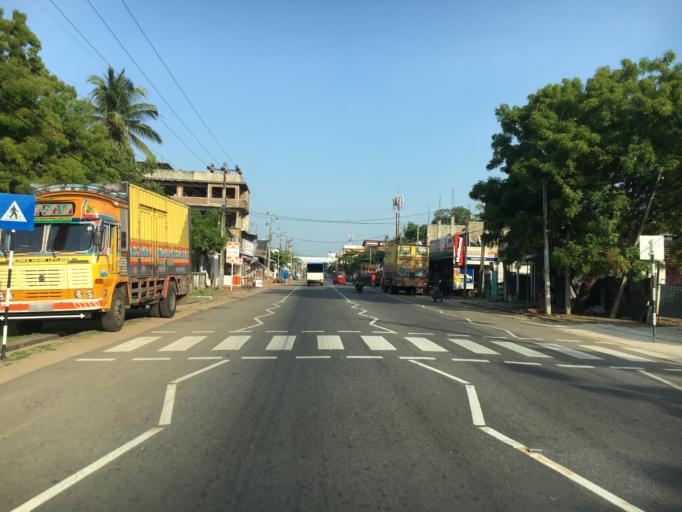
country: LK
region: Eastern Province
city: Eravur Town
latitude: 7.9122
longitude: 81.5270
